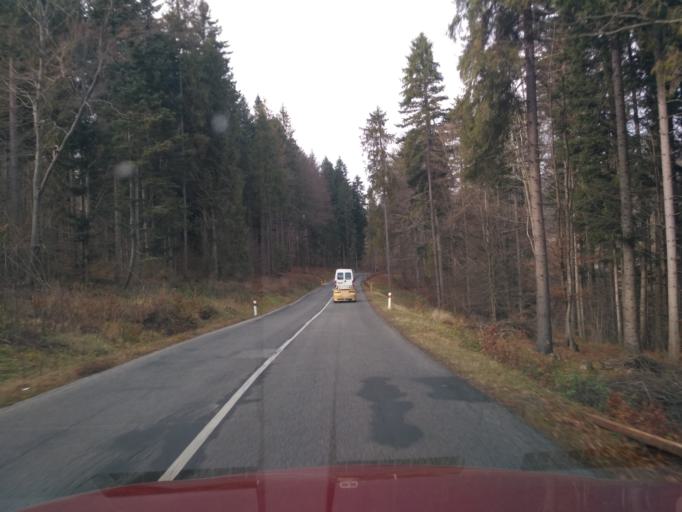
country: SK
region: Kosicky
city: Medzev
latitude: 48.7934
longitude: 20.7502
